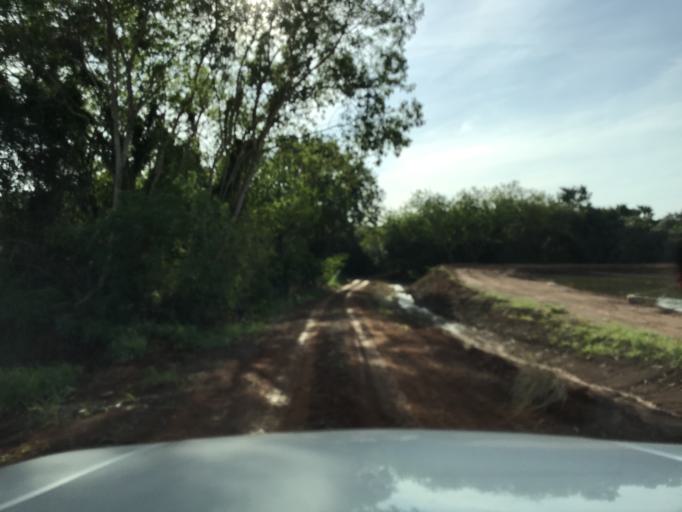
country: BR
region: Parana
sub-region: Palotina
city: Palotina
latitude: -24.2525
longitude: -53.7543
